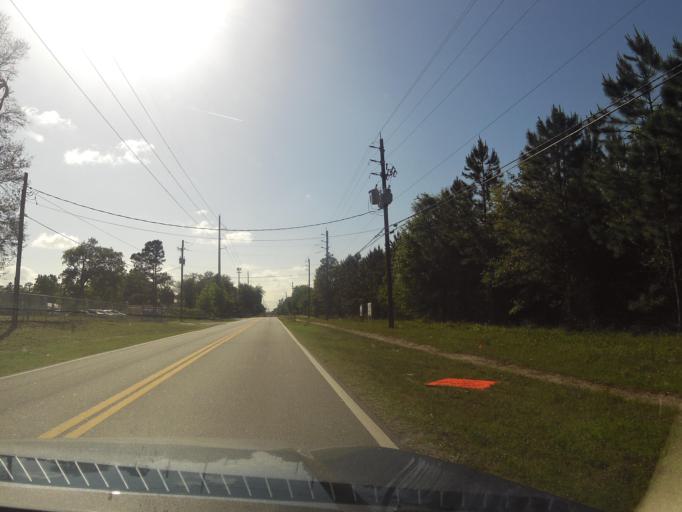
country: US
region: Florida
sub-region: Duval County
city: Jacksonville
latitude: 30.4345
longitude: -81.5661
